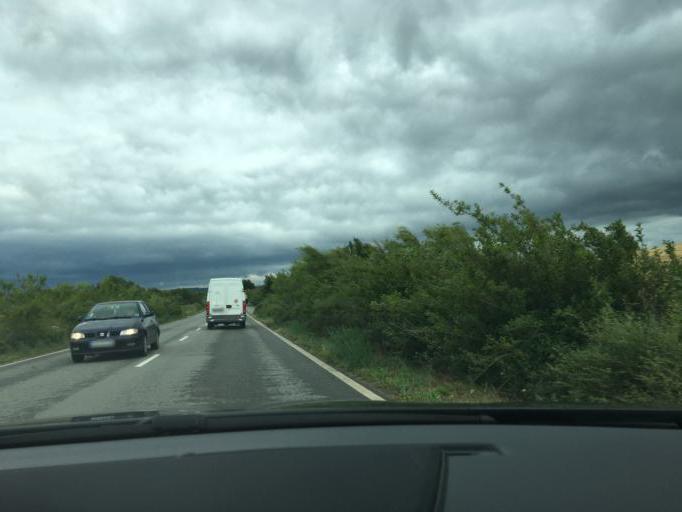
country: BG
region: Kyustendil
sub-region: Obshtina Bobovdol
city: Bobovdol
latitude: 42.2733
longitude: 23.0173
